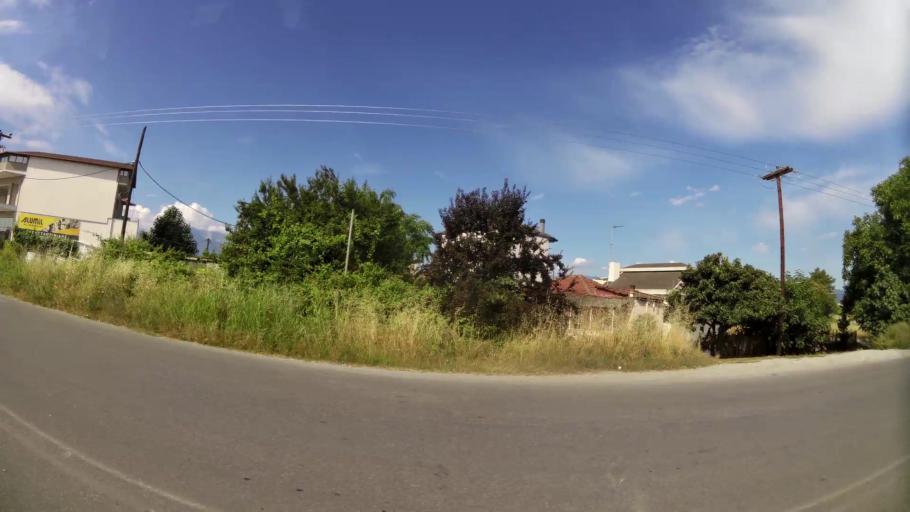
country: GR
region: Central Macedonia
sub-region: Nomos Pierias
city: Katerini
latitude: 40.2788
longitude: 22.5182
